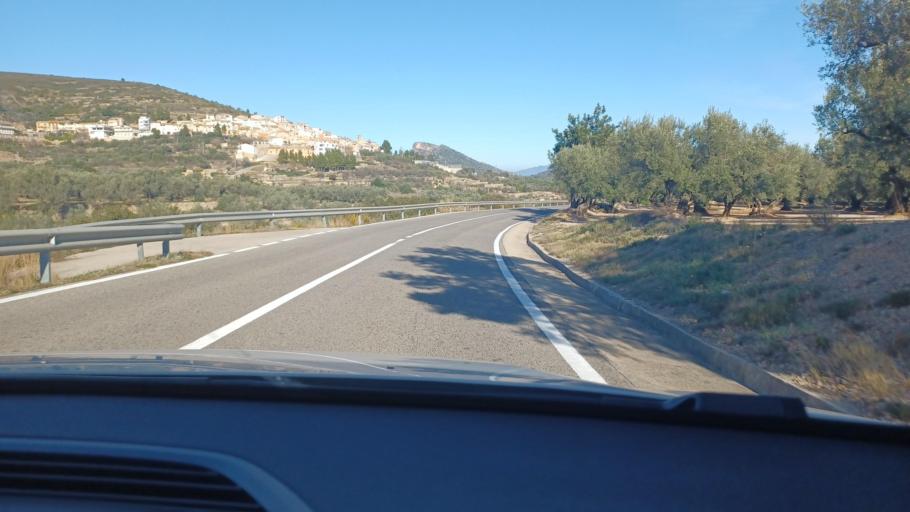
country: ES
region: Catalonia
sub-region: Provincia de Tarragona
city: Mas de Barberans
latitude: 40.7277
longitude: 0.3717
